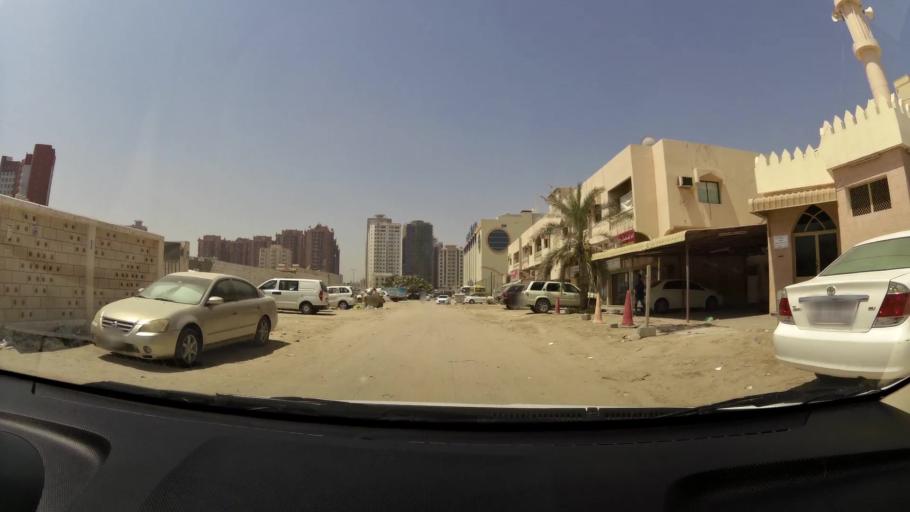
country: AE
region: Ajman
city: Ajman
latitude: 25.3918
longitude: 55.4595
